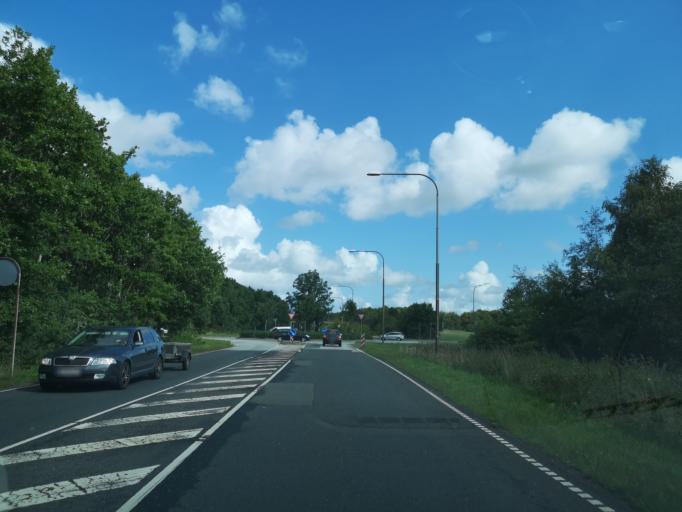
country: DK
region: Central Jutland
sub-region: Holstebro Kommune
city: Holstebro
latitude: 56.3732
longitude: 8.5876
